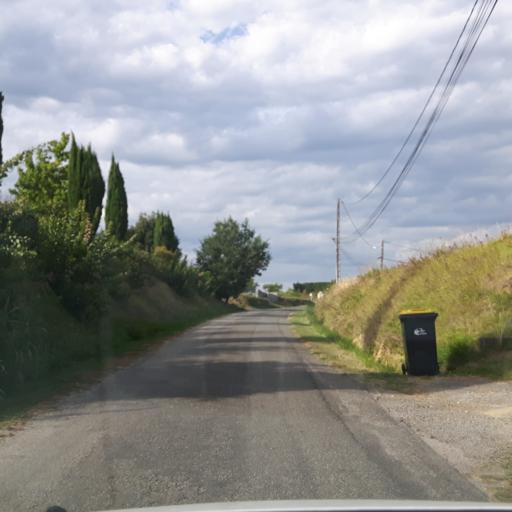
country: FR
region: Midi-Pyrenees
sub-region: Departement de la Haute-Garonne
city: Castelnau-d'Estretefonds
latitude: 43.7848
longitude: 1.3709
